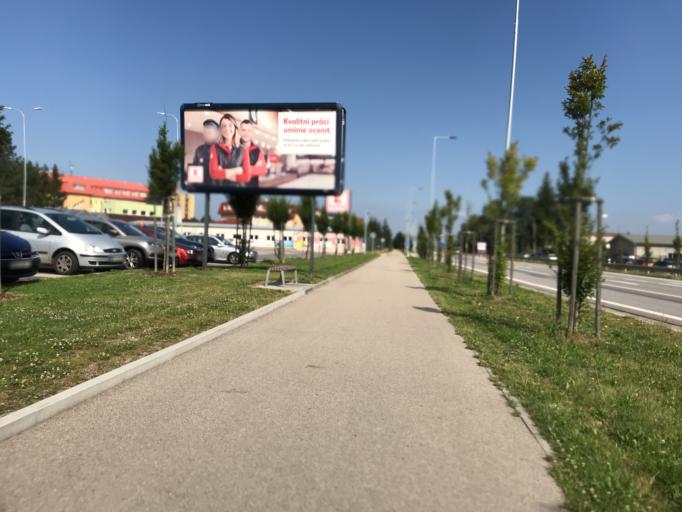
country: CZ
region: Jihocesky
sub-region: Okres Jindrichuv Hradec
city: Trebon
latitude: 49.0106
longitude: 14.7602
